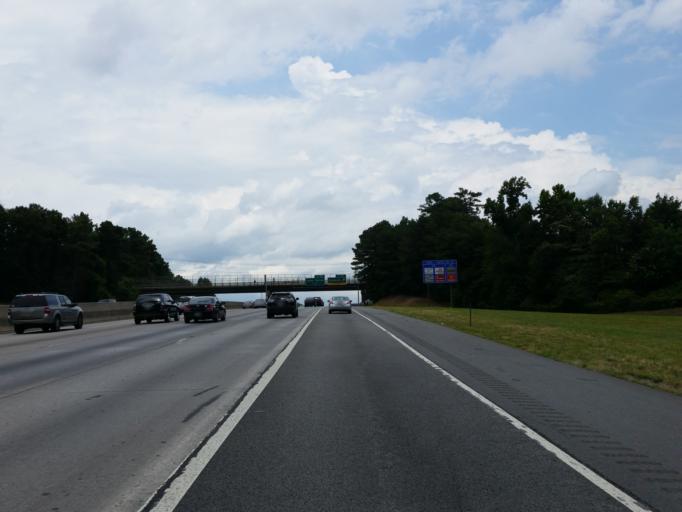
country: US
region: Georgia
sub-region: Fulton County
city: Sandy Springs
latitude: 33.9278
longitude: -84.3576
